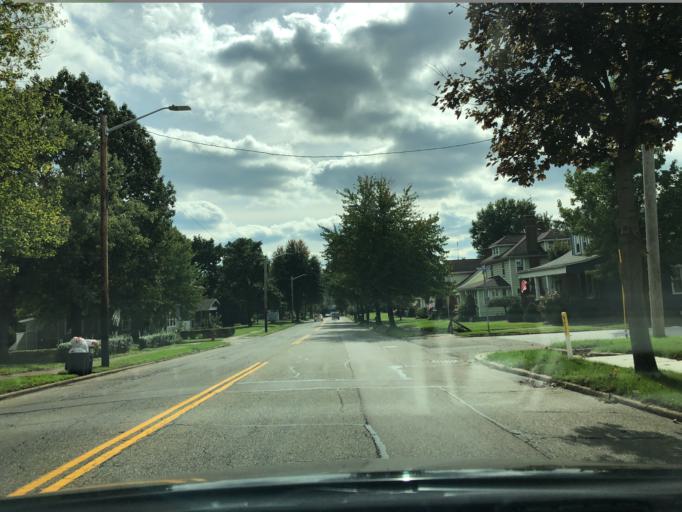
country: US
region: Ohio
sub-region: Stark County
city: Brewster
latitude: 40.7197
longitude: -81.5973
